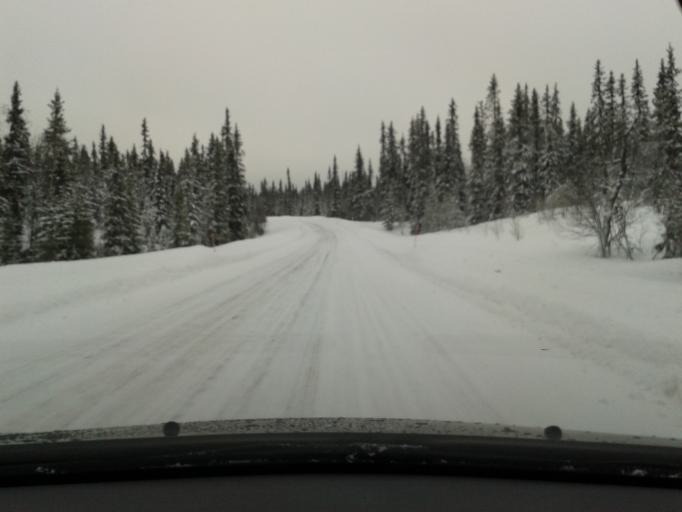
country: SE
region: Vaesterbotten
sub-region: Vilhelmina Kommun
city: Sjoberg
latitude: 65.1216
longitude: 15.8772
